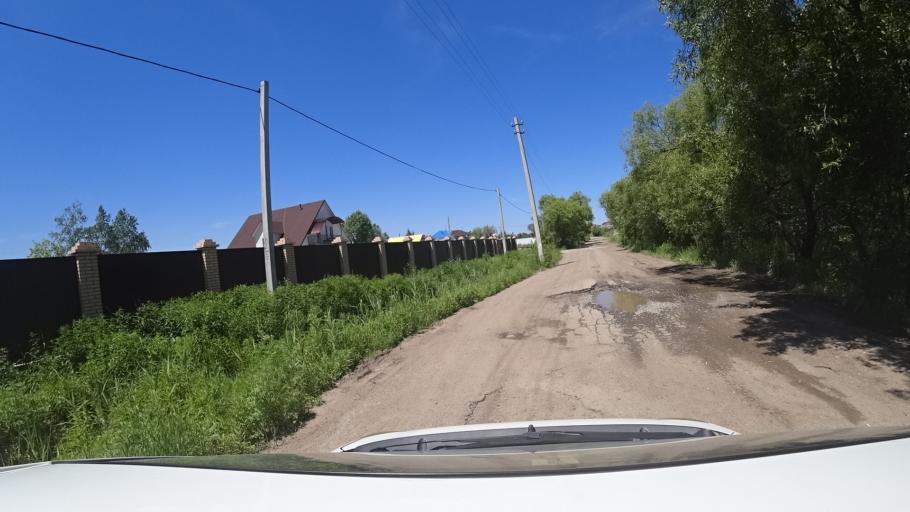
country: RU
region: Khabarovsk Krai
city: Topolevo
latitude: 48.4992
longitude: 135.1831
